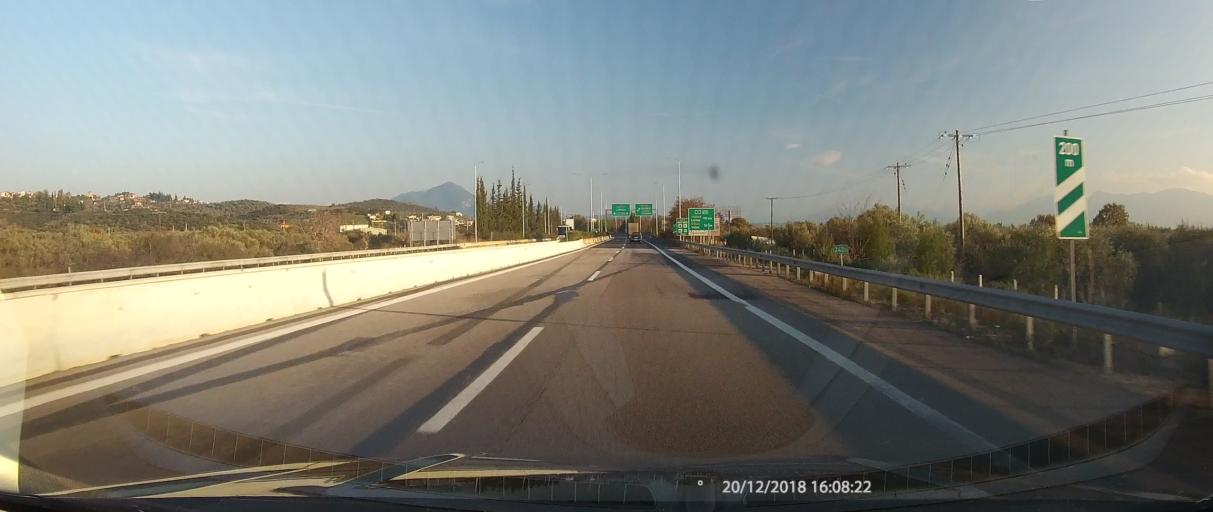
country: GR
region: Central Greece
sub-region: Nomos Fthiotidos
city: Pelasgia
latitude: 38.8863
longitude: 22.7638
